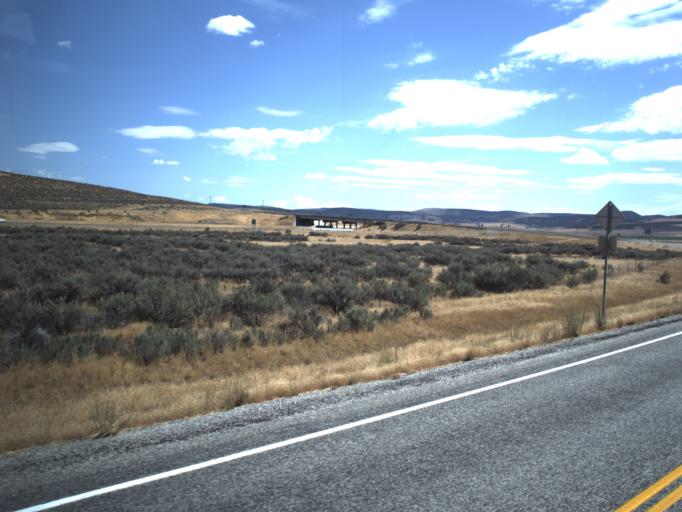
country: US
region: Idaho
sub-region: Oneida County
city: Malad City
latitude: 41.9642
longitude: -112.7649
